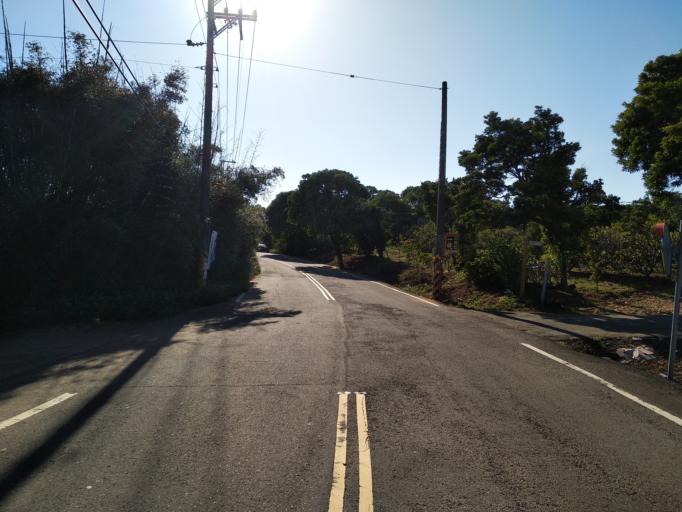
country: TW
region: Taiwan
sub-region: Hsinchu
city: Zhubei
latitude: 24.8734
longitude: 121.0734
